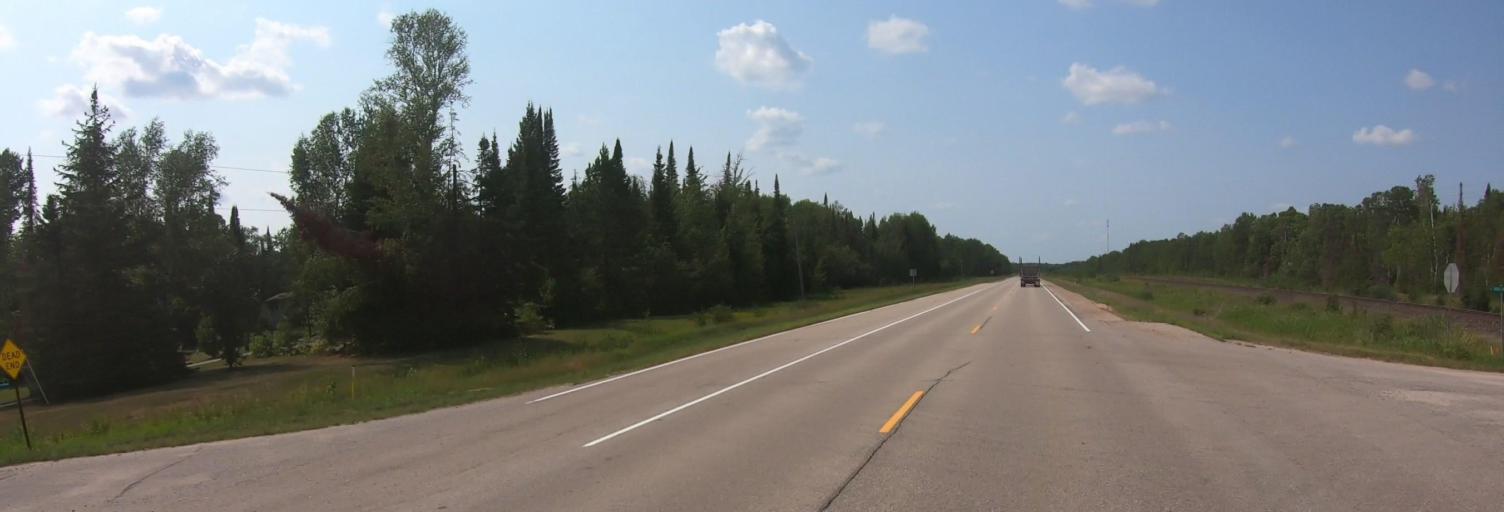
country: US
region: Minnesota
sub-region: Roseau County
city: Warroad
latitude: 48.7937
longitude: -95.0685
